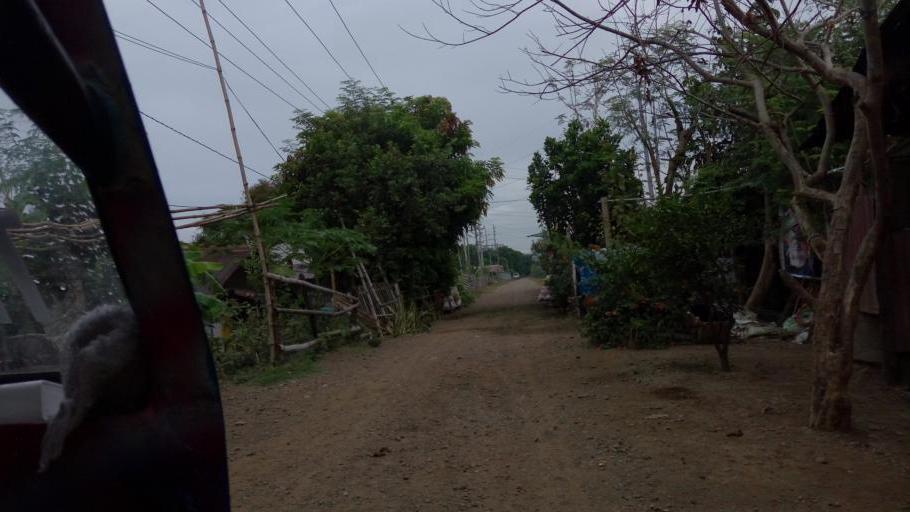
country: PH
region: Ilocos
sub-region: Province of La Union
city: Paringao
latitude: 16.5551
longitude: 120.3255
